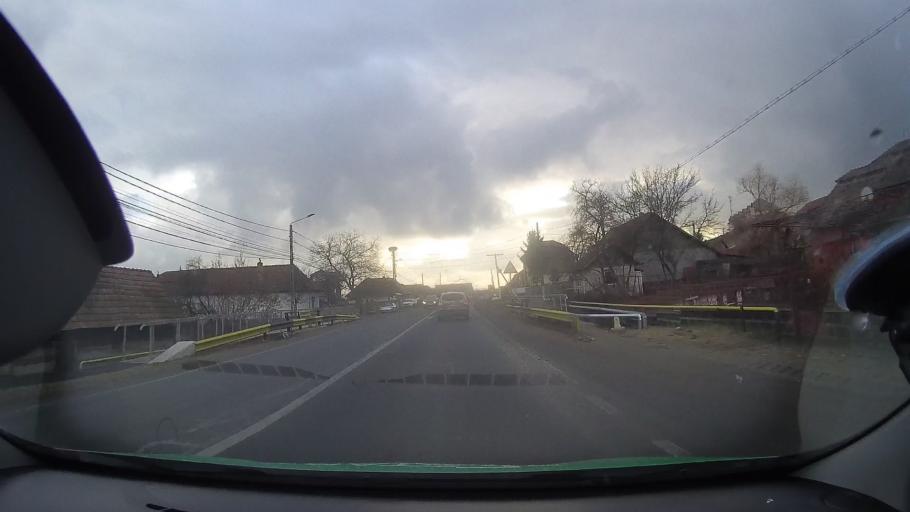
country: RO
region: Cluj
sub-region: Comuna Luna
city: Luncani
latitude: 46.5048
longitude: 23.9196
